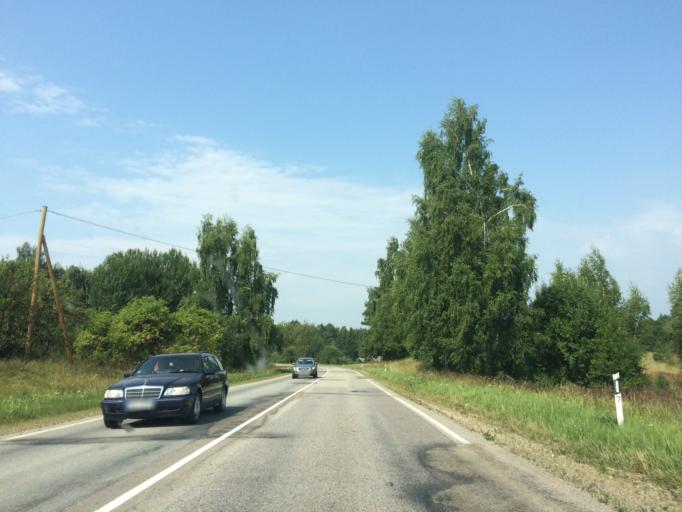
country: LV
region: Ludzas Rajons
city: Ludza
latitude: 56.5377
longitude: 27.5768
